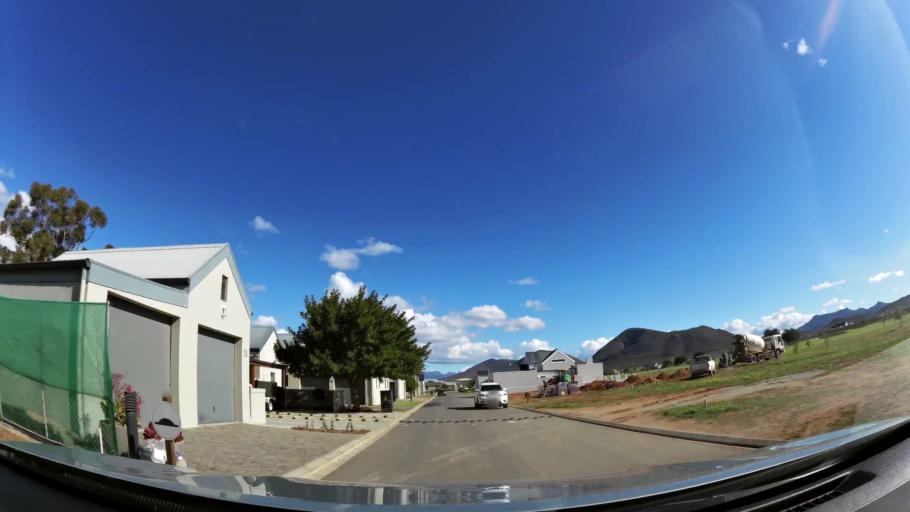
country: ZA
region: Western Cape
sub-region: Cape Winelands District Municipality
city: Ashton
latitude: -33.8114
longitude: 19.8499
